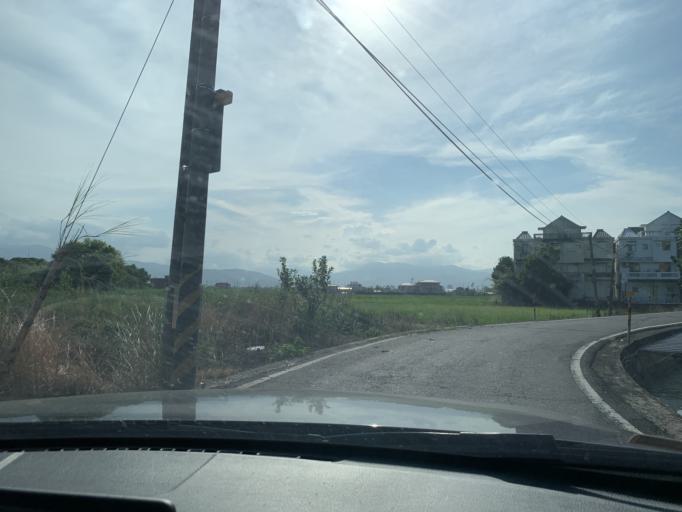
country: TW
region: Taiwan
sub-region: Yilan
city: Yilan
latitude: 24.6781
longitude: 121.8094
